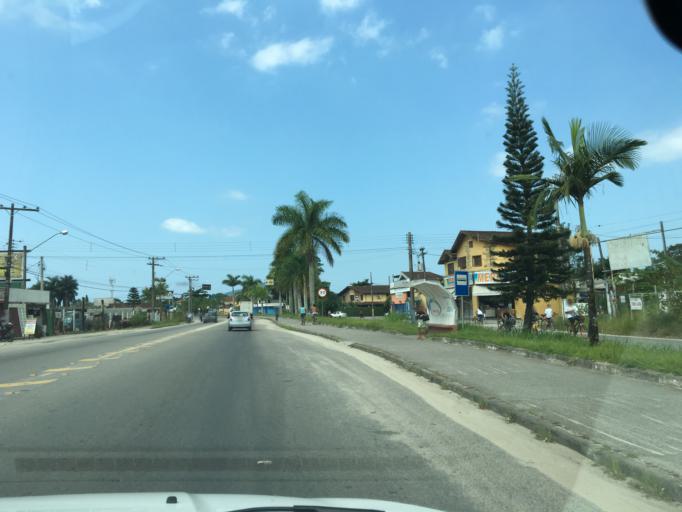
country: BR
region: Sao Paulo
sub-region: Ubatuba
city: Ubatuba
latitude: -23.4378
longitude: -45.0951
